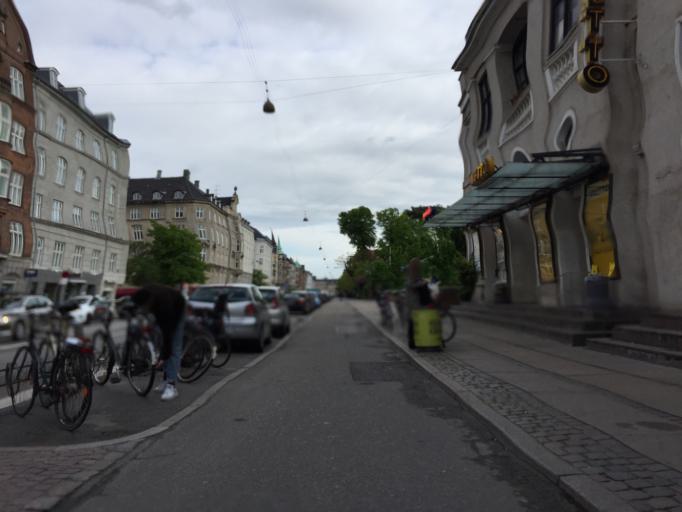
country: DK
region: Capital Region
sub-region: Kobenhavn
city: Copenhagen
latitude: 55.7041
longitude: 12.5773
